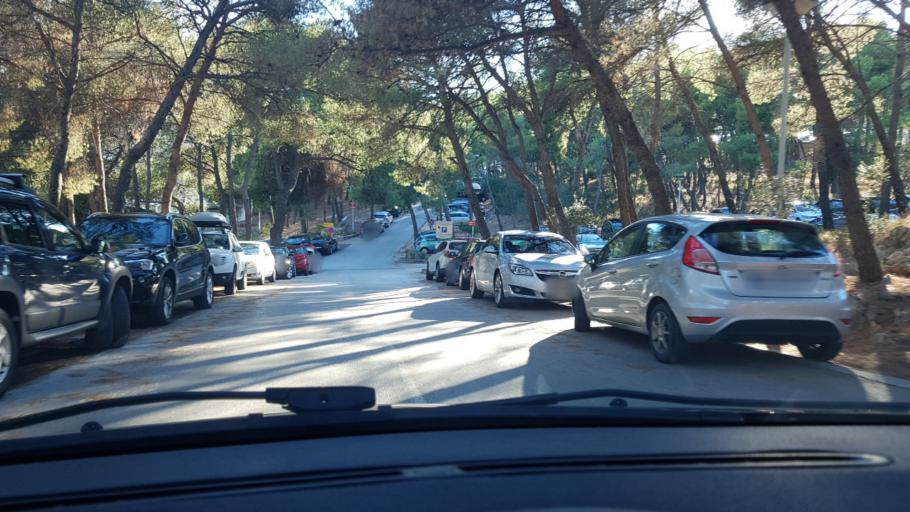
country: HR
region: Splitsko-Dalmatinska
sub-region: Grad Trogir
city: Trogir
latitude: 43.5141
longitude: 16.2094
